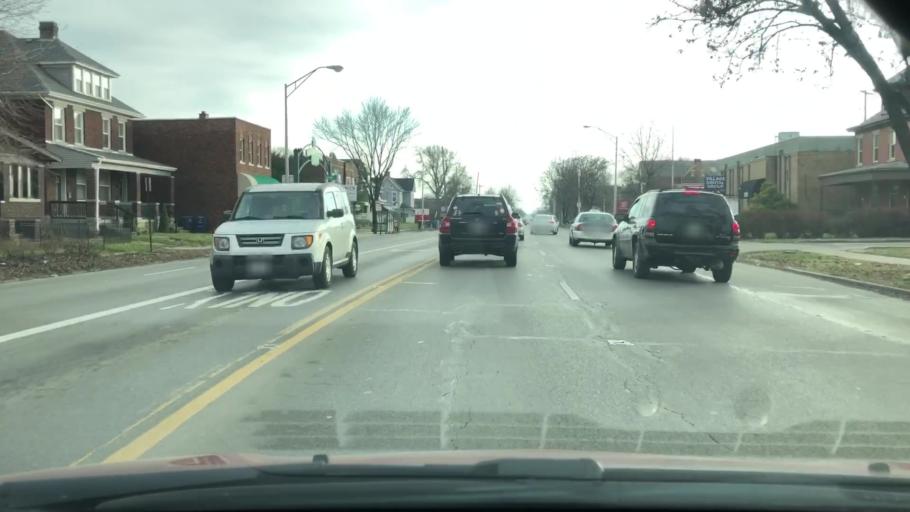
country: US
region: Ohio
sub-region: Franklin County
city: Columbus
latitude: 39.9393
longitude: -82.9962
